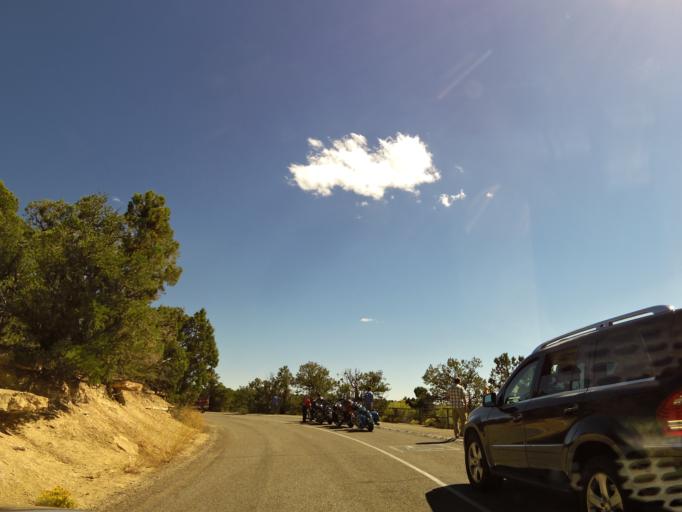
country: US
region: Colorado
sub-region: Montezuma County
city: Cortez
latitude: 37.1670
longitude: -108.4928
